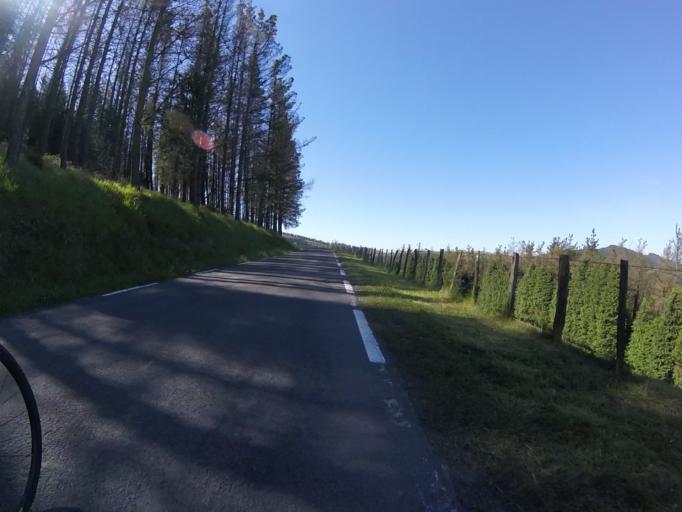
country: ES
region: Basque Country
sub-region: Provincia de Guipuzcoa
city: Errezil
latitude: 43.2097
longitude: -2.2011
